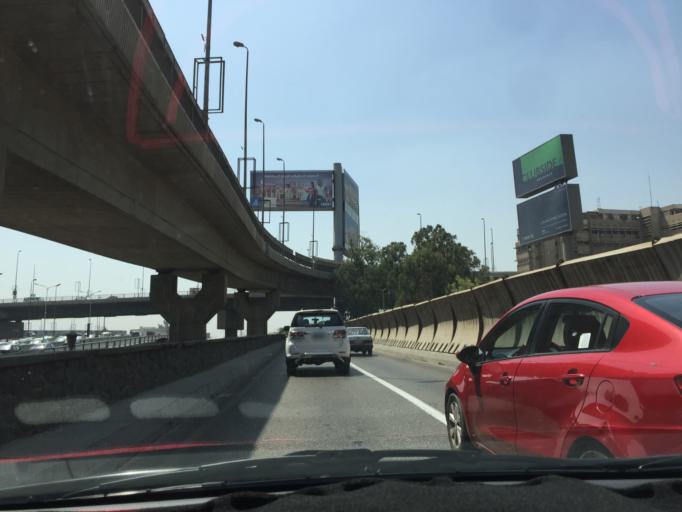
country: EG
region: Muhafazat al Qahirah
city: Cairo
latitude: 30.0704
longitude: 31.2929
